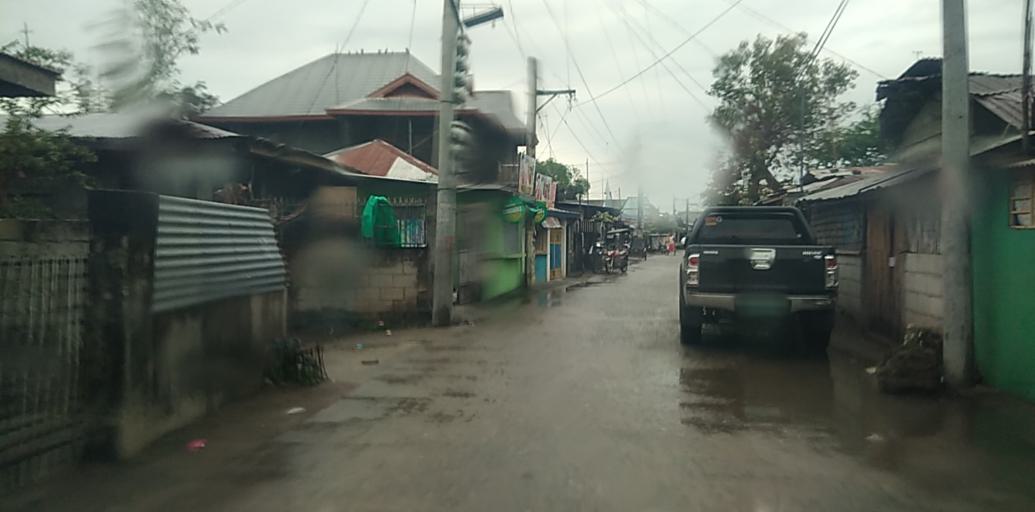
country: PH
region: Central Luzon
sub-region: Province of Pampanga
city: Arayat
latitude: 15.1363
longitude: 120.7403
